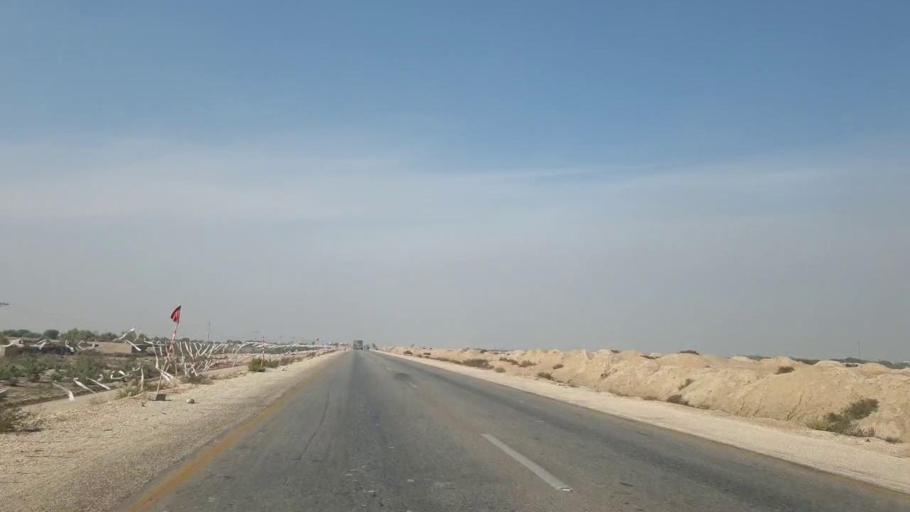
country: PK
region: Sindh
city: Sann
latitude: 25.9450
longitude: 68.2006
